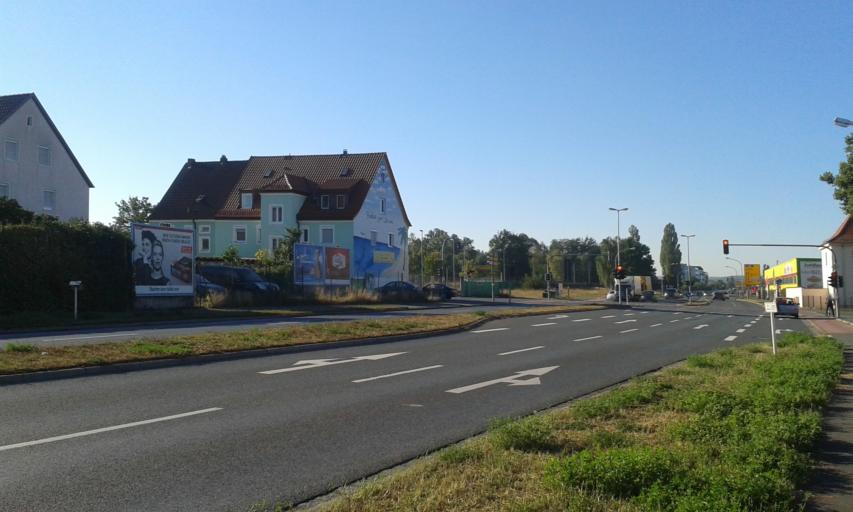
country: DE
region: Bavaria
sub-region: Upper Franconia
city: Bamberg
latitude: 49.8906
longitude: 10.9220
